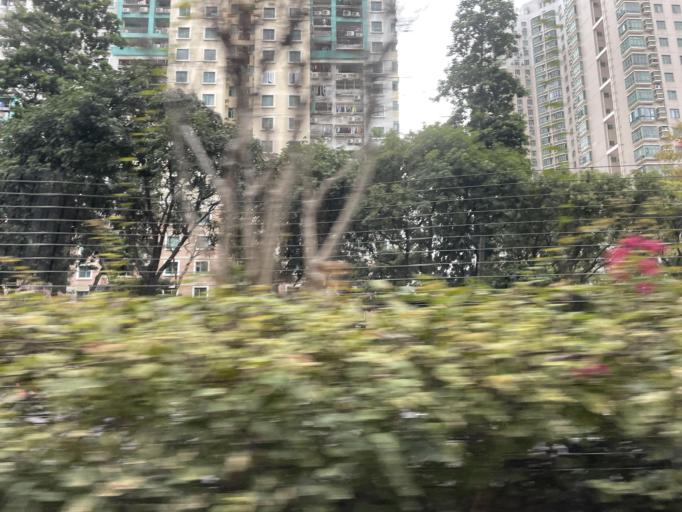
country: CN
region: Guangdong
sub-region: Shenzhen
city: Shenzhen
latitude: 22.5202
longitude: 114.0437
